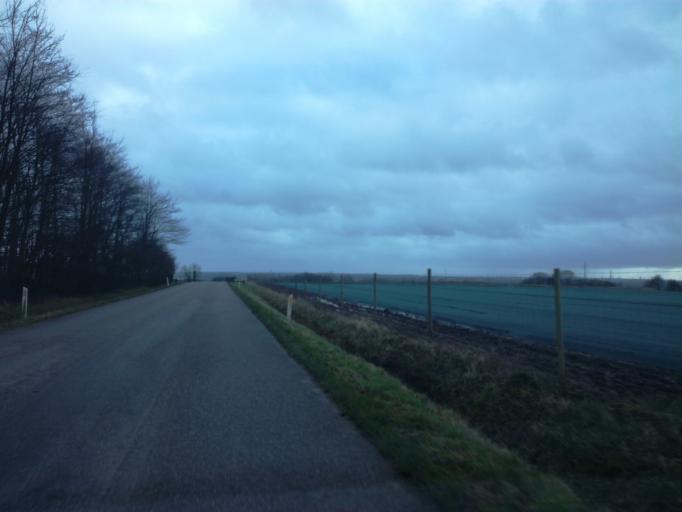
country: DK
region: South Denmark
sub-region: Vejle Kommune
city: Brejning
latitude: 55.6339
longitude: 9.6973
